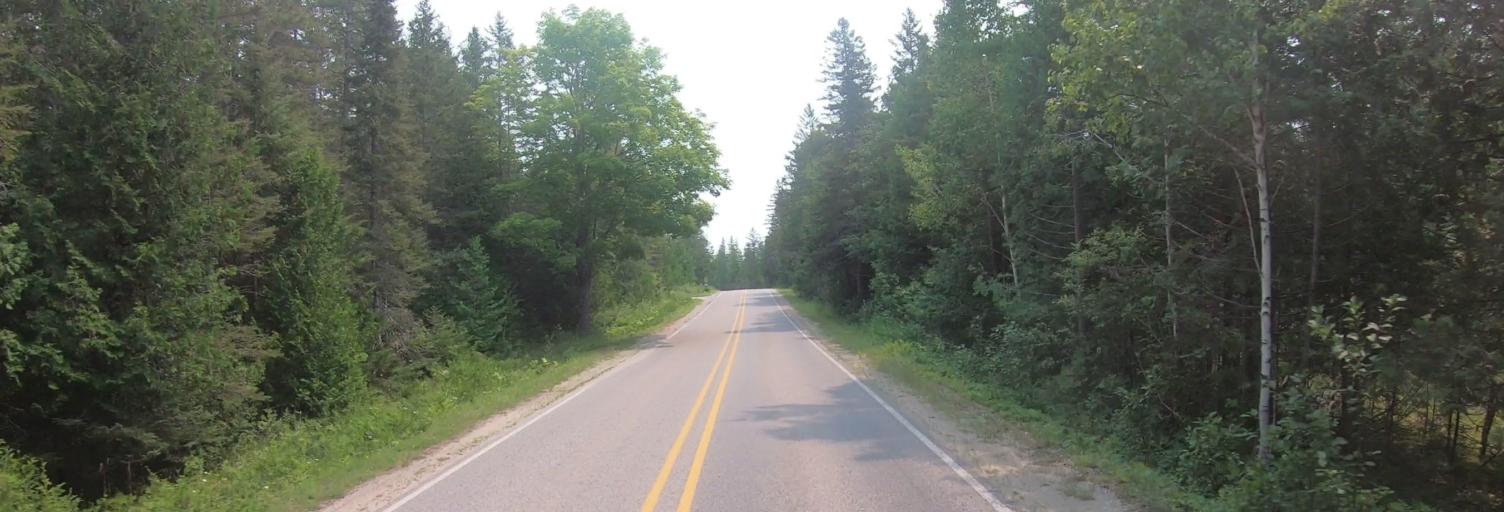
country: CA
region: Ontario
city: Thessalon
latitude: 45.9696
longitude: -83.6457
